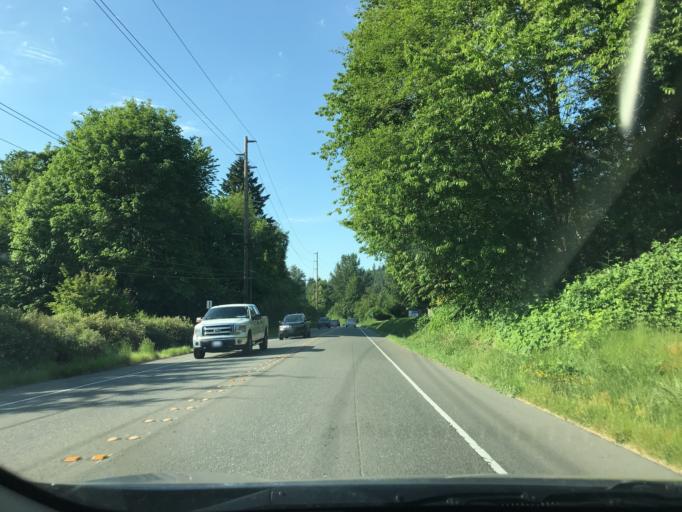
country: US
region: Washington
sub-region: King County
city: Issaquah
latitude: 47.5103
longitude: -122.0232
